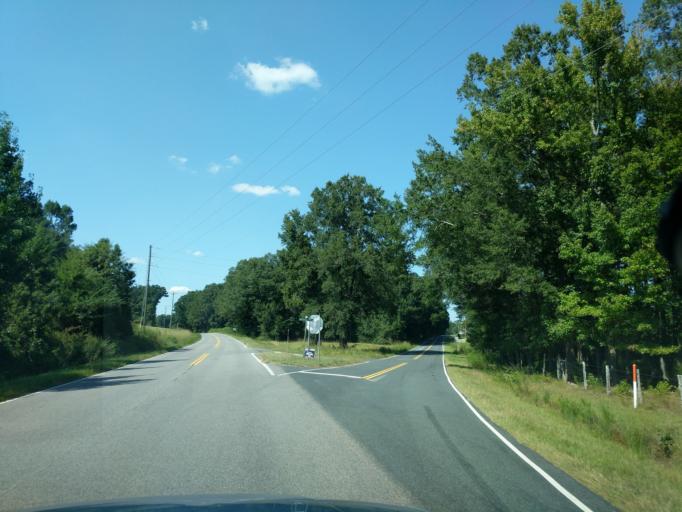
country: US
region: South Carolina
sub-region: Lexington County
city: Leesville
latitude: 34.0041
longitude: -81.5148
